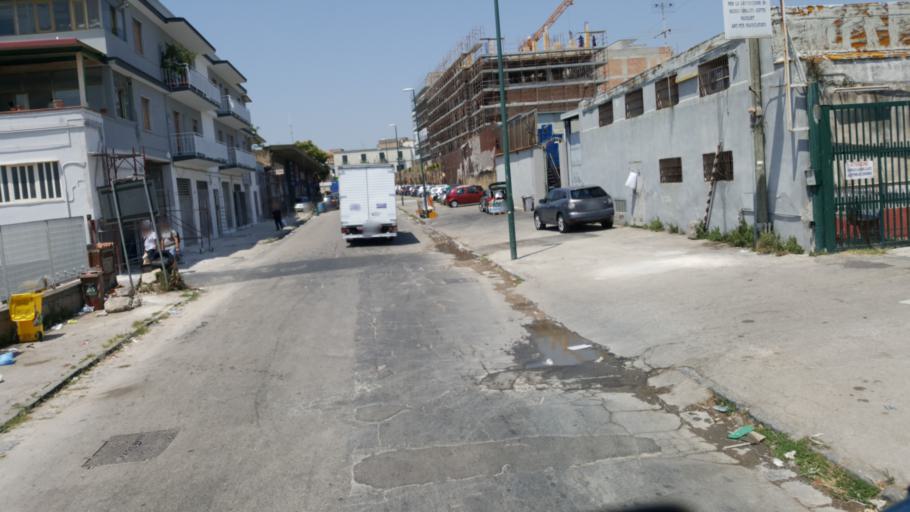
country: IT
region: Campania
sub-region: Provincia di Napoli
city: Arpino
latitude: 40.8736
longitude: 14.3078
